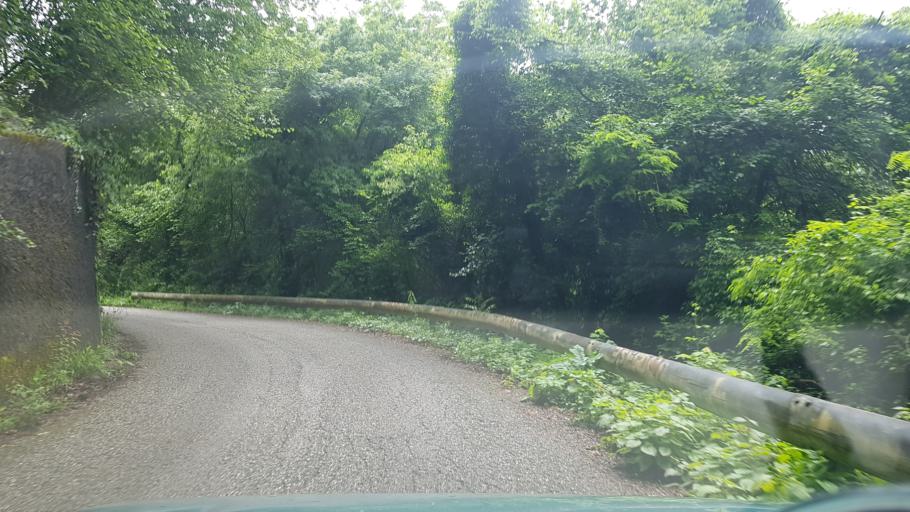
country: IT
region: Friuli Venezia Giulia
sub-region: Provincia di Gorizia
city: San Floriano del Collio
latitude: 45.9547
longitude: 13.5950
